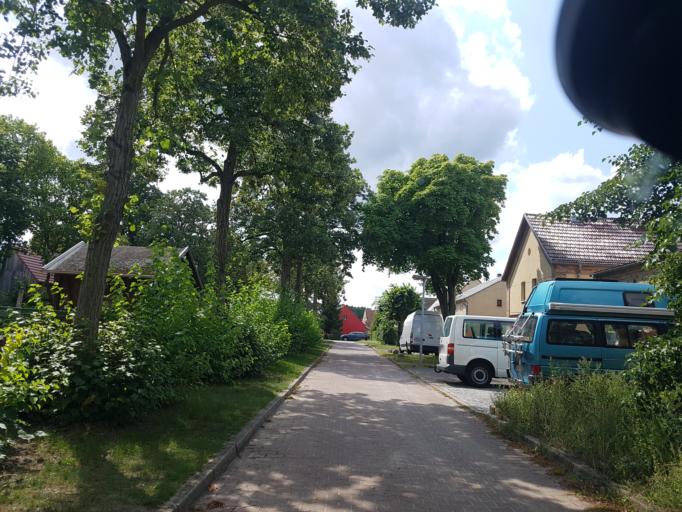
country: DE
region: Brandenburg
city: Borkwalde
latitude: 52.2891
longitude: 12.8389
